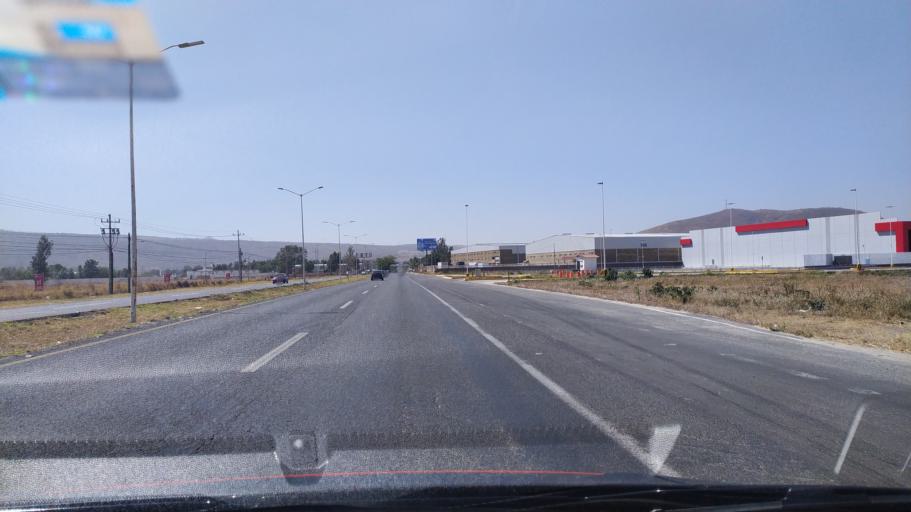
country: MX
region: Jalisco
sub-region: Tlajomulco de Zuniga
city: Santa Cruz de las Flores
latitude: 20.4612
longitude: -103.5128
